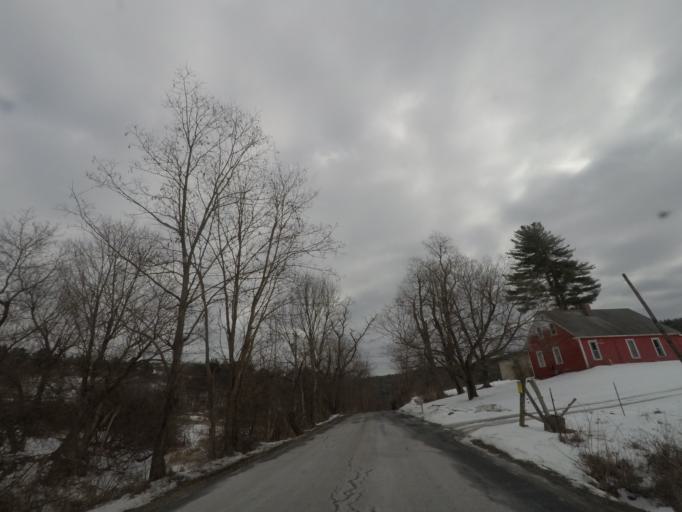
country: US
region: New York
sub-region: Rensselaer County
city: Hoosick Falls
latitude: 42.8686
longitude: -73.3886
